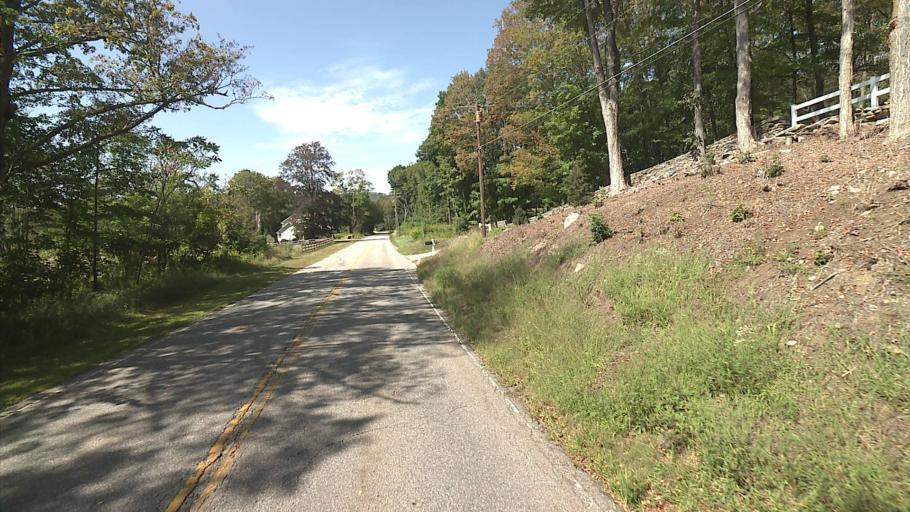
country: US
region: Connecticut
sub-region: Windham County
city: Willimantic
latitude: 41.6709
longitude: -72.2638
